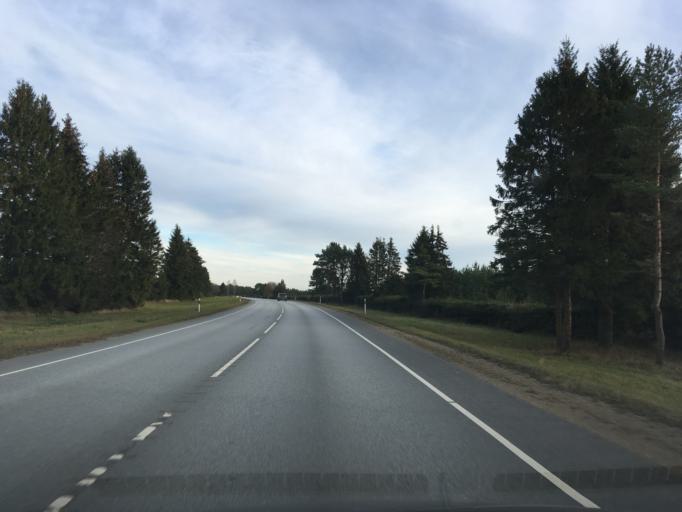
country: EE
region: Laeaene-Virumaa
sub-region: Viru-Nigula vald
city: Kunda
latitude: 59.3858
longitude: 26.6136
